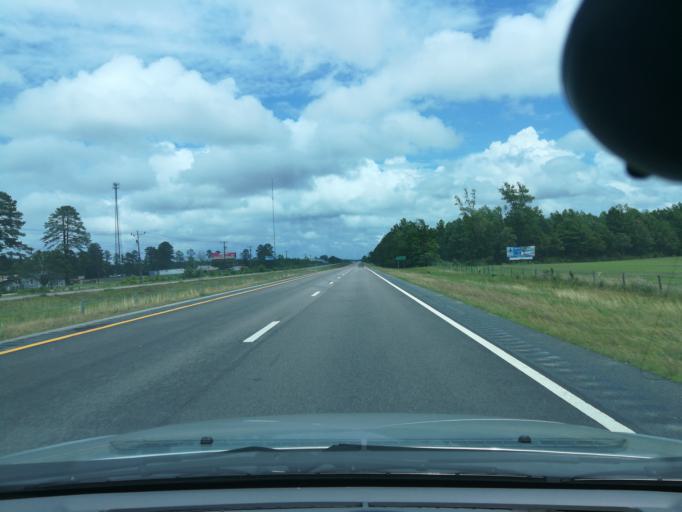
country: US
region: North Carolina
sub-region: Tyrrell County
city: Columbia
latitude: 35.8823
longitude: -76.3704
